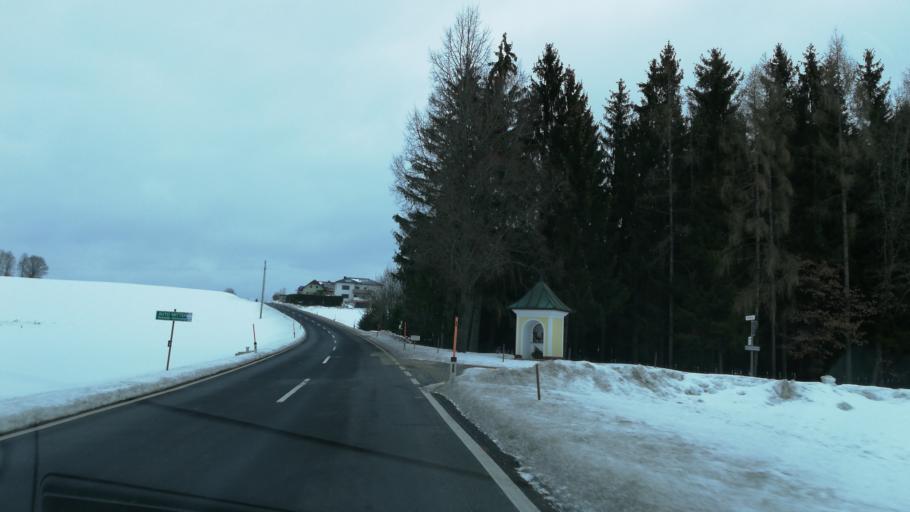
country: AT
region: Upper Austria
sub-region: Politischer Bezirk Urfahr-Umgebung
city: Herzogsdorf
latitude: 48.4468
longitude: 14.1216
